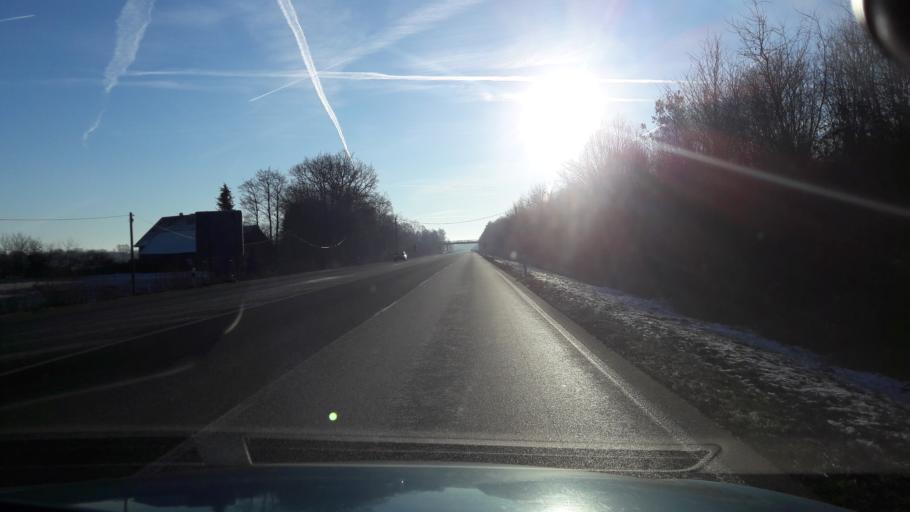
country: DE
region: North Rhine-Westphalia
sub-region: Regierungsbezirk Arnsberg
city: Lippstadt
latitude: 51.7238
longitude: 8.3368
